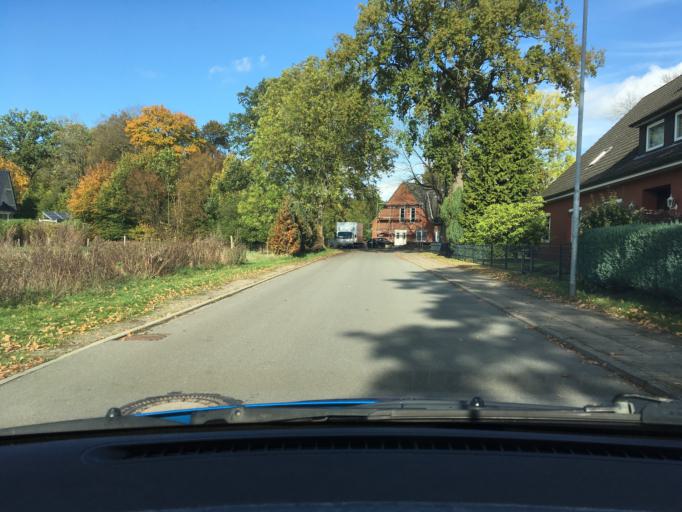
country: DE
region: Lower Saxony
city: Kakenstorf
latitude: 53.3178
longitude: 9.7938
